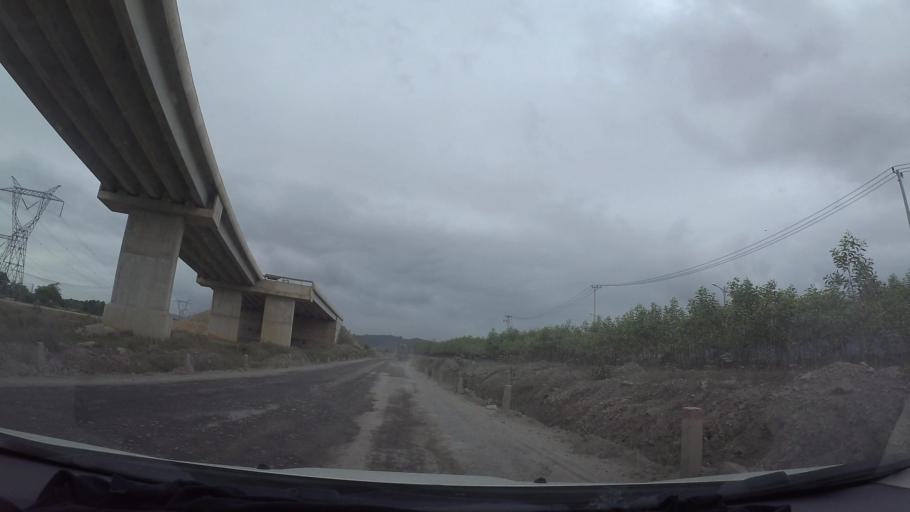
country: VN
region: Da Nang
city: Lien Chieu
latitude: 16.0970
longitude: 108.0892
